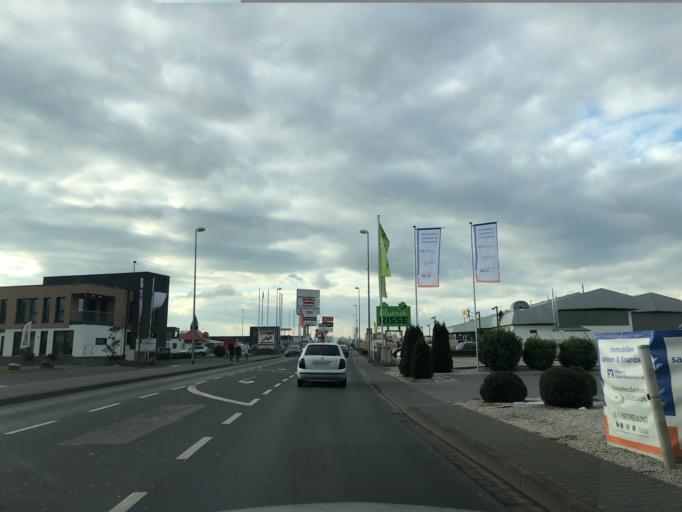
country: DE
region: Rheinland-Pfalz
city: Urmitz
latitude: 50.3963
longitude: 7.5210
